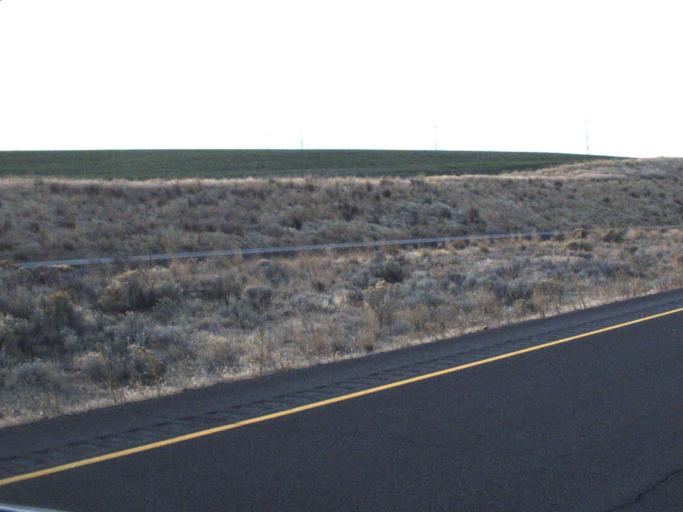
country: US
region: Washington
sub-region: Adams County
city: Ritzville
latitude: 46.9435
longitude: -118.5810
